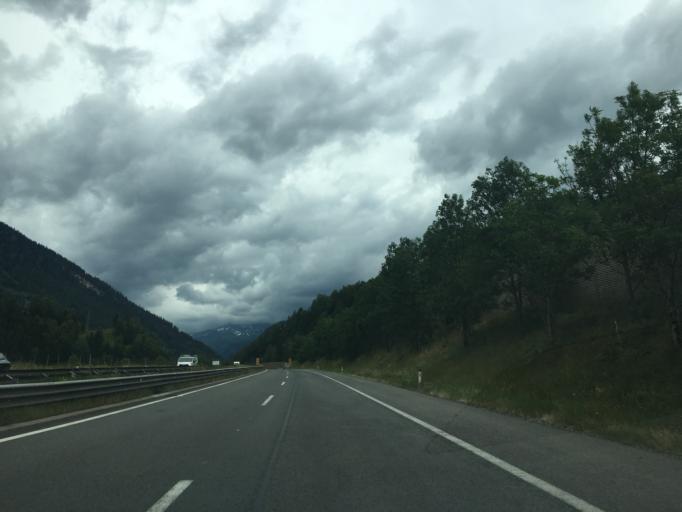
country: AT
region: Salzburg
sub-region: Politischer Bezirk Tamsweg
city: Zederhaus
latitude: 47.1249
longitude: 13.5629
